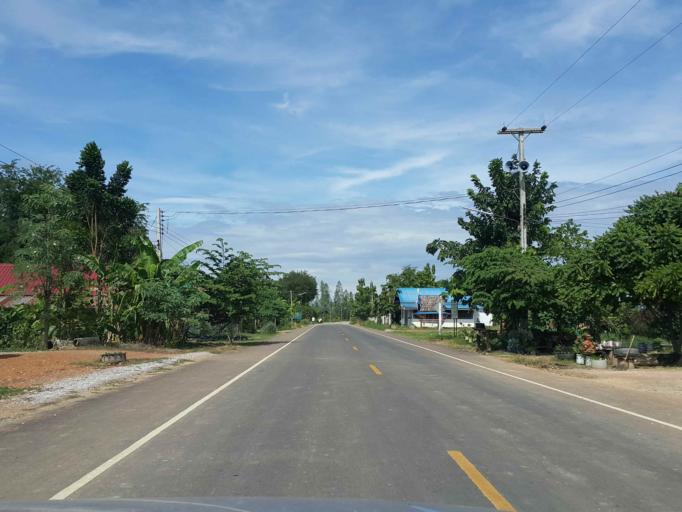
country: TH
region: Sukhothai
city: Ban Dan Lan Hoi
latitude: 17.1132
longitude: 99.5098
